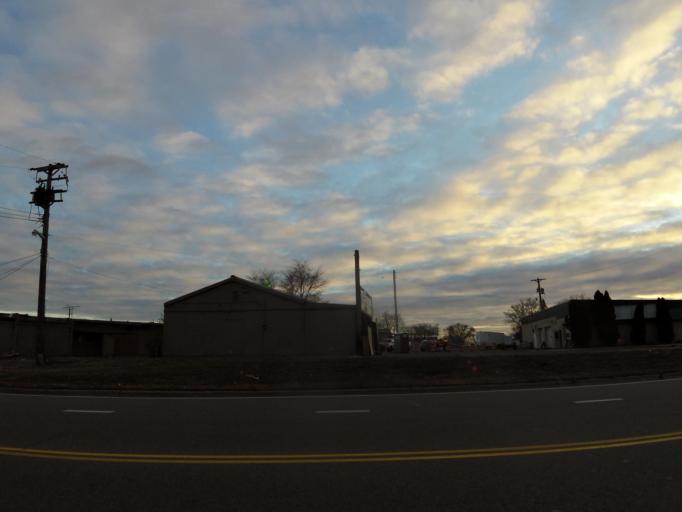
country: US
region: Minnesota
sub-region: Ramsey County
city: Vadnais Heights
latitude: 45.0504
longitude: -93.0353
